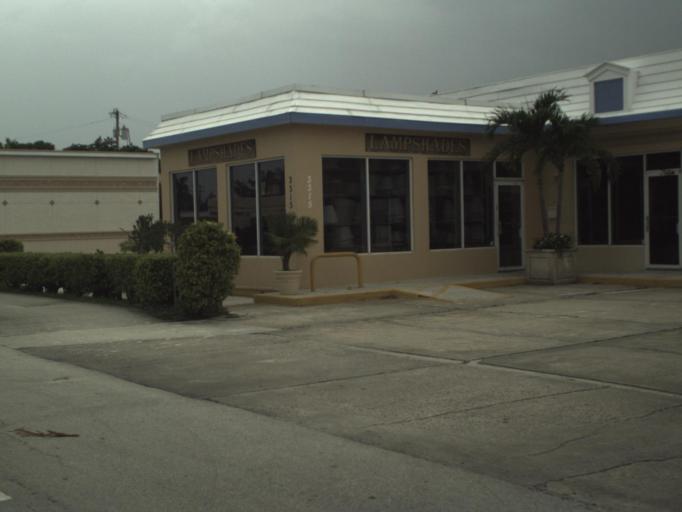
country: US
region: Florida
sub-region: Palm Beach County
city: Palm Beach
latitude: 26.6823
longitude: -80.0546
